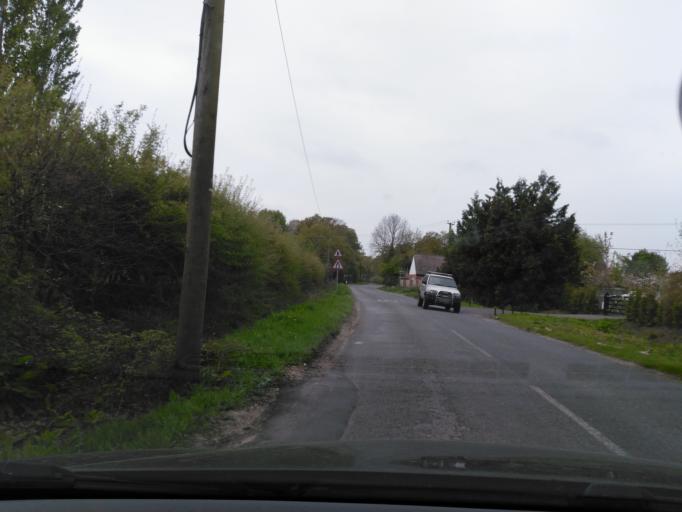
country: GB
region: England
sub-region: Hampshire
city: Tadley
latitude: 51.3262
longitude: -1.1072
